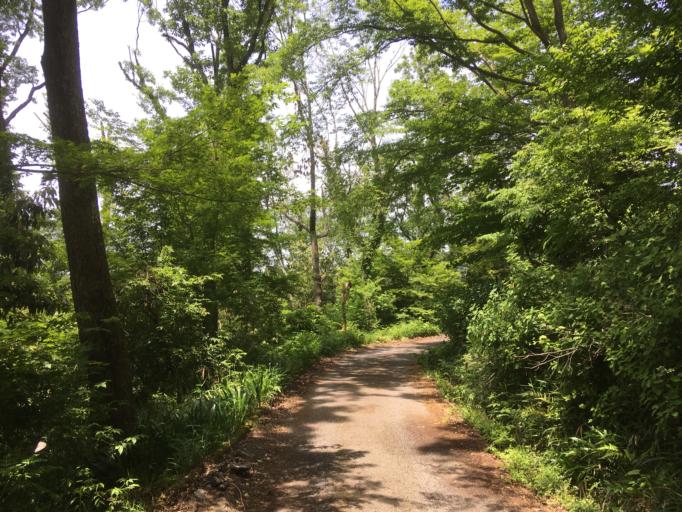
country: JP
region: Nara
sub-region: Ikoma-shi
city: Ikoma
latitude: 34.6667
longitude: 135.6658
